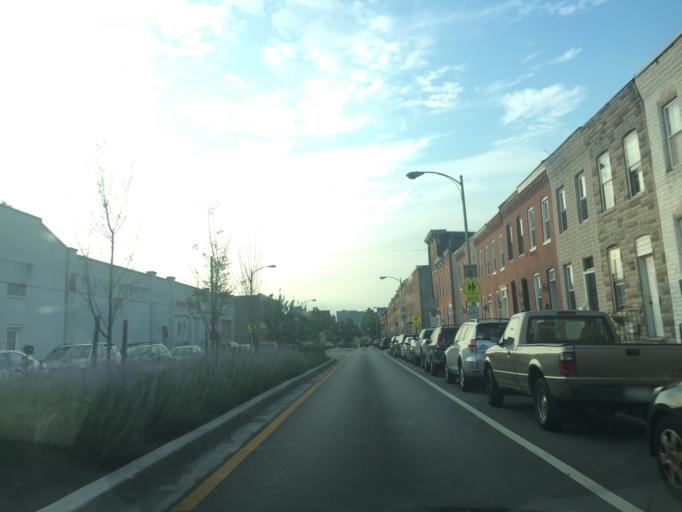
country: US
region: Maryland
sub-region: City of Baltimore
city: Baltimore
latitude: 39.2688
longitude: -76.6150
